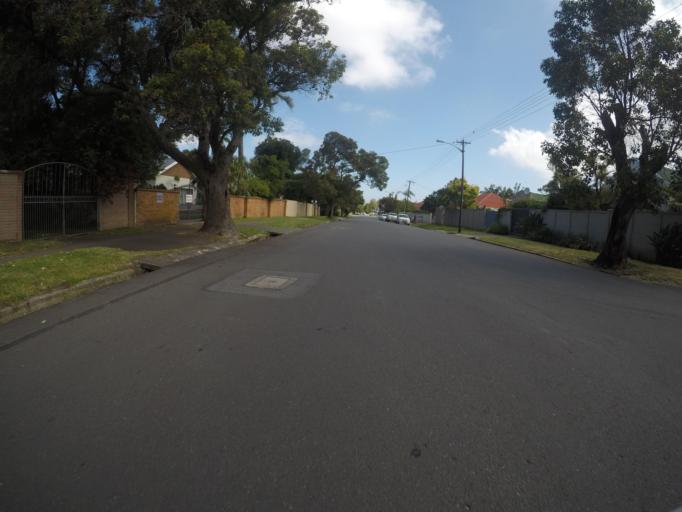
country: ZA
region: Eastern Cape
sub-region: Buffalo City Metropolitan Municipality
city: East London
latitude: -32.9766
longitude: 27.9025
